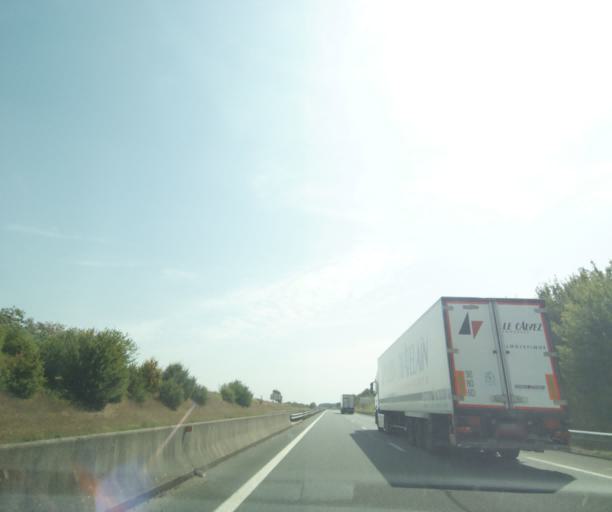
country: FR
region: Pays de la Loire
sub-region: Departement de la Vendee
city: Sainte-Hermine
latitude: 46.5309
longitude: -1.0702
